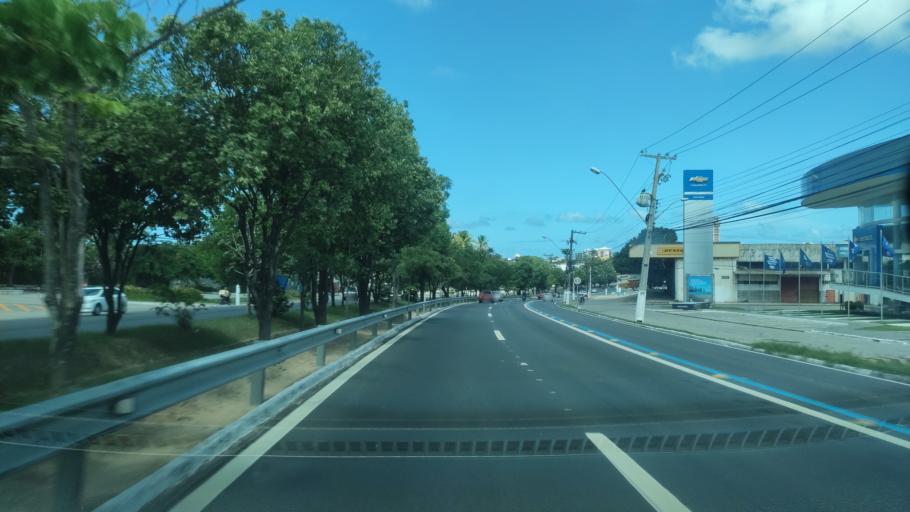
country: BR
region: Alagoas
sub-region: Maceio
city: Maceio
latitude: -9.6049
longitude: -35.7427
